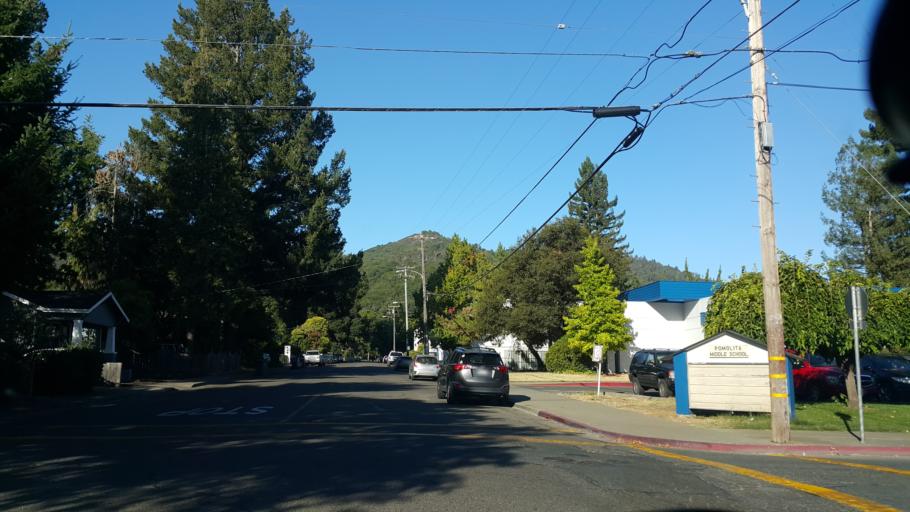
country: US
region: California
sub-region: Mendocino County
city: Ukiah
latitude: 39.1545
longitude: -123.2158
